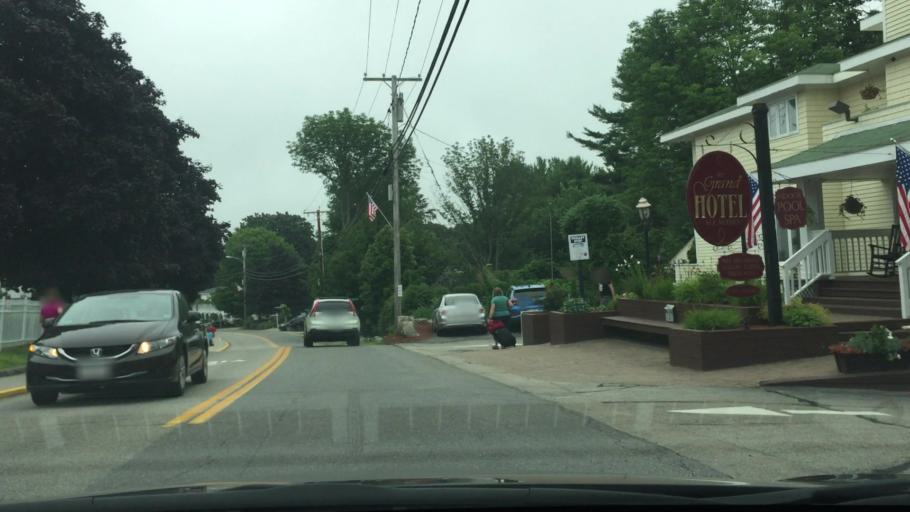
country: US
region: Maine
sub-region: York County
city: Ogunquit
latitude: 43.2405
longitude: -70.5963
